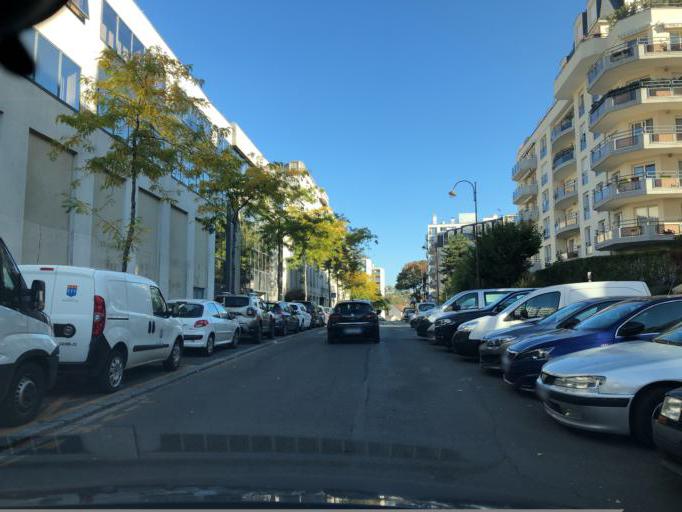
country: FR
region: Ile-de-France
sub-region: Departement des Hauts-de-Seine
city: Chaville
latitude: 48.8125
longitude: 2.1931
